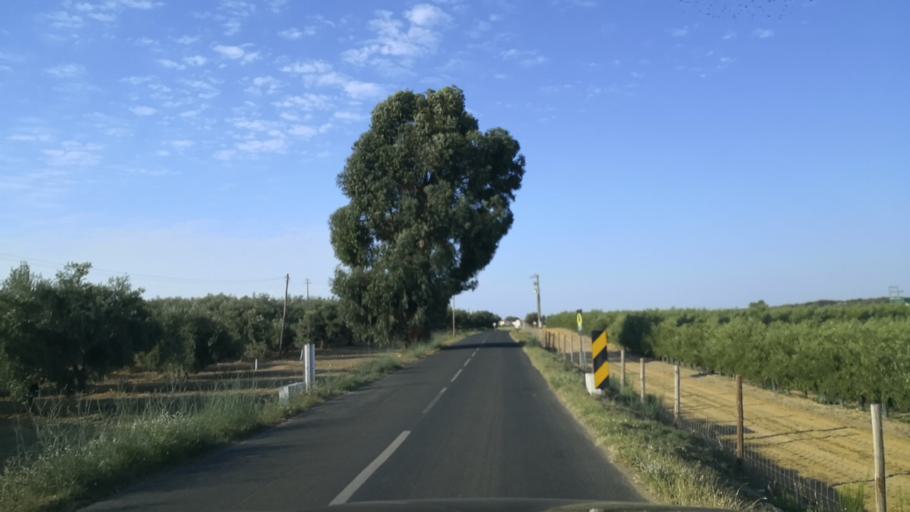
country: PT
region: Santarem
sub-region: Santarem
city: Santarem
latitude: 39.2773
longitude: -8.6598
